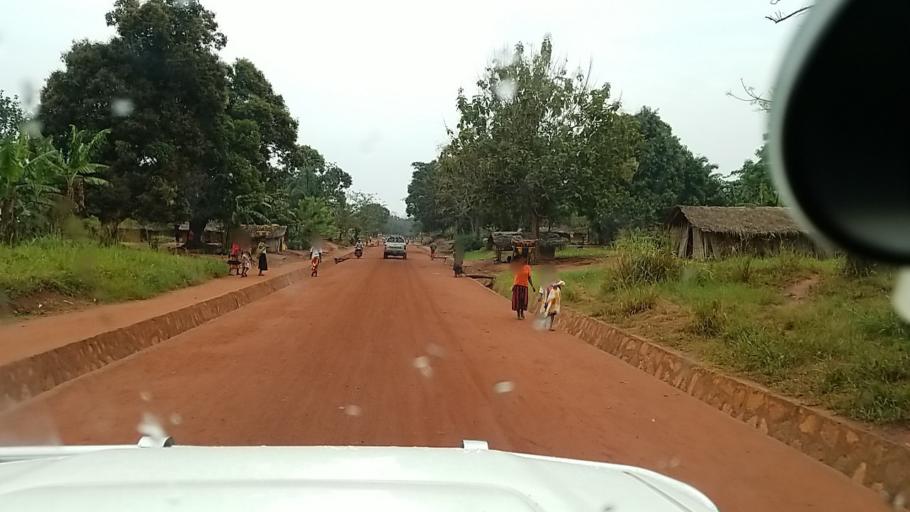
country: CD
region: Equateur
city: Gemena
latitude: 3.2222
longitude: 19.7773
